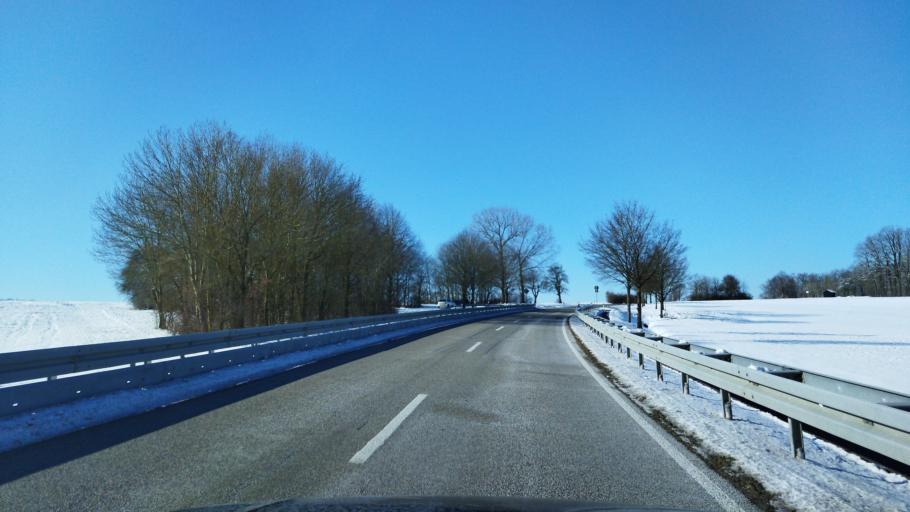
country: DE
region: Baden-Wuerttemberg
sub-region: Regierungsbezirk Stuttgart
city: Langenburg
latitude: 49.2450
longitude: 9.8796
